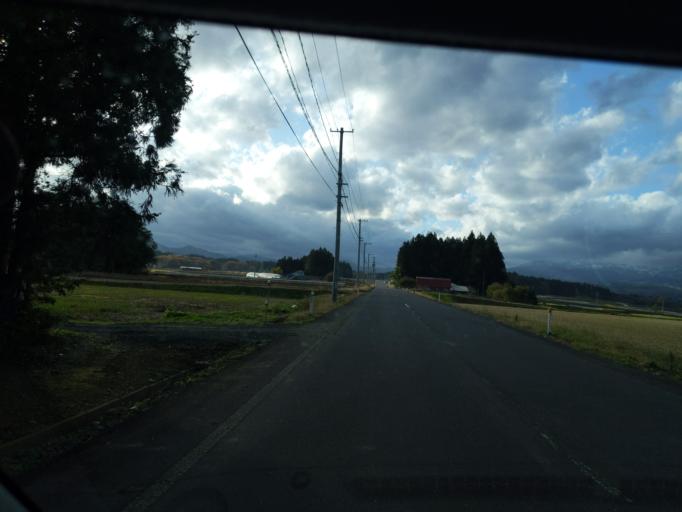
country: JP
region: Iwate
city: Mizusawa
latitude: 39.1083
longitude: 141.0192
